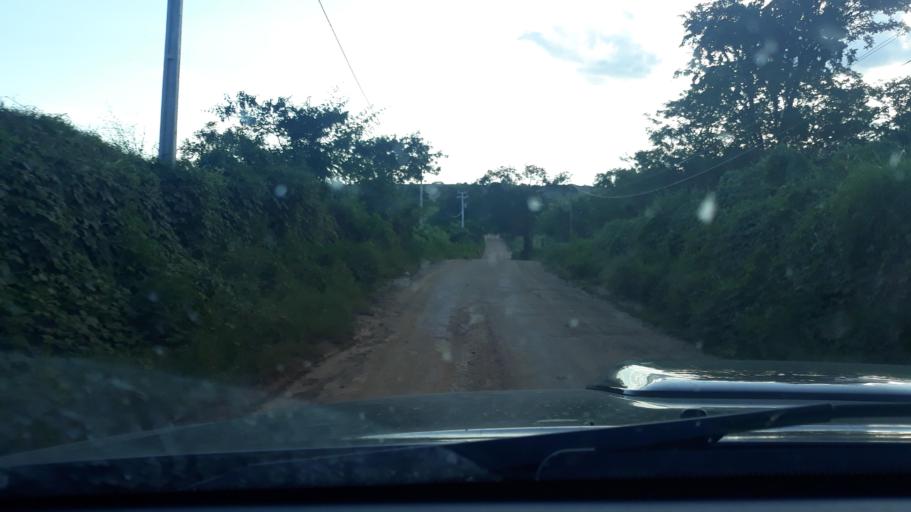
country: BR
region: Bahia
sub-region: Riacho De Santana
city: Riacho de Santana
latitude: -13.8053
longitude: -42.7132
